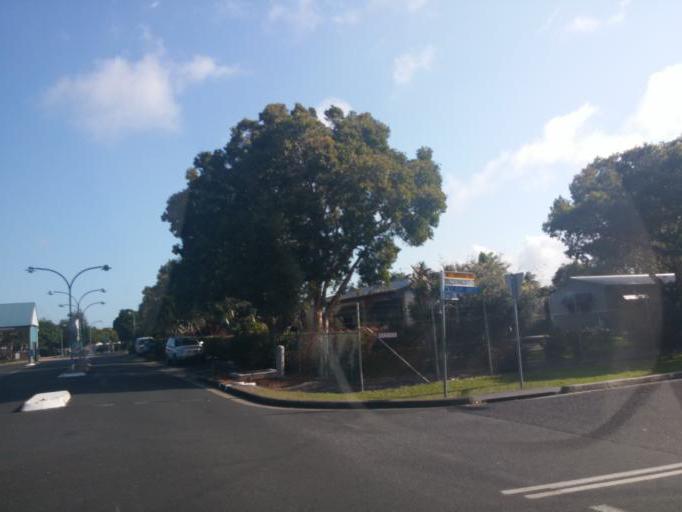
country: AU
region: New South Wales
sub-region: Coffs Harbour
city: Coffs Harbour
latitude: -30.2922
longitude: 153.1378
